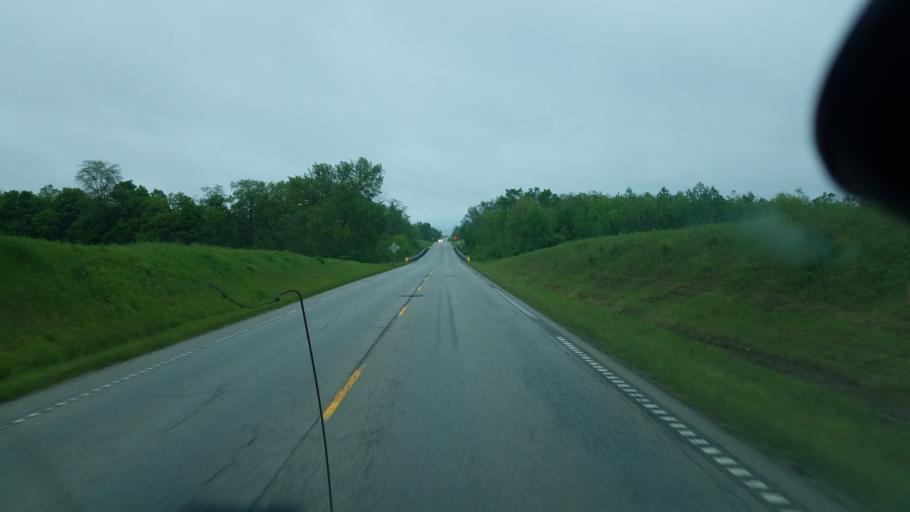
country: US
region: Ohio
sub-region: Highland County
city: Leesburg
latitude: 39.2962
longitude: -83.5862
